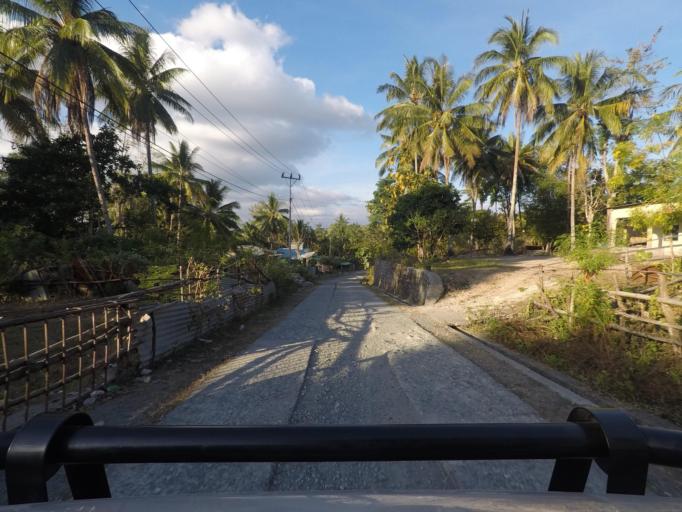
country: TL
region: Bobonaro
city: Maliana
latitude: -8.9684
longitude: 125.0459
